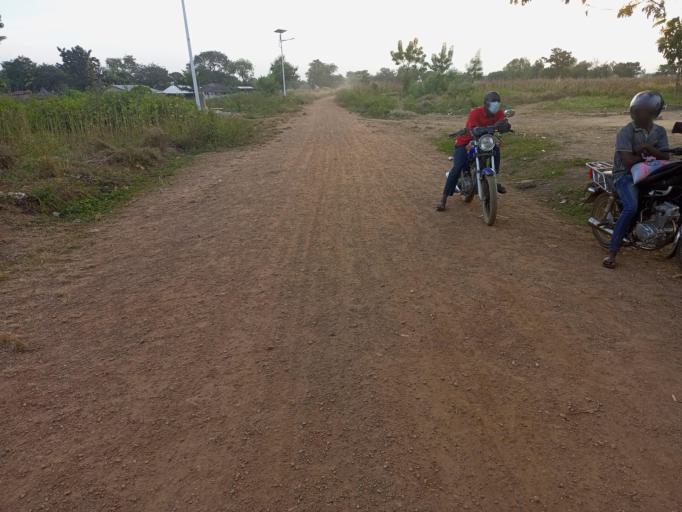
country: TG
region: Kara
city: Niamtougou
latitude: 9.6914
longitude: 0.9311
